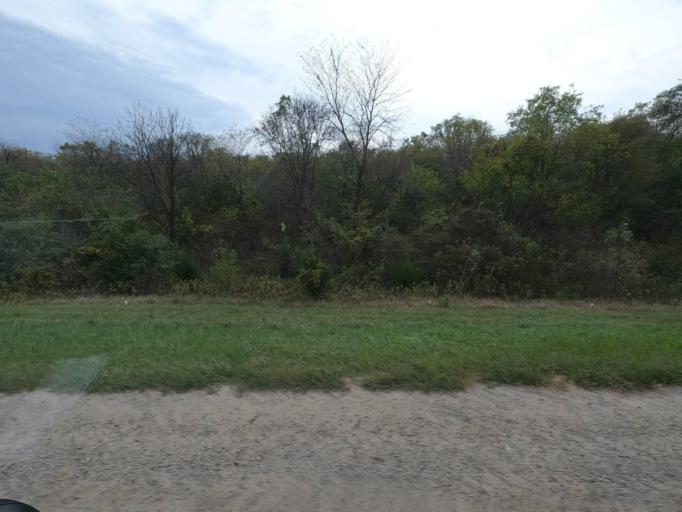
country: US
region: Iowa
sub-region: Van Buren County
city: Keosauqua
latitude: 40.8657
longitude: -92.1424
